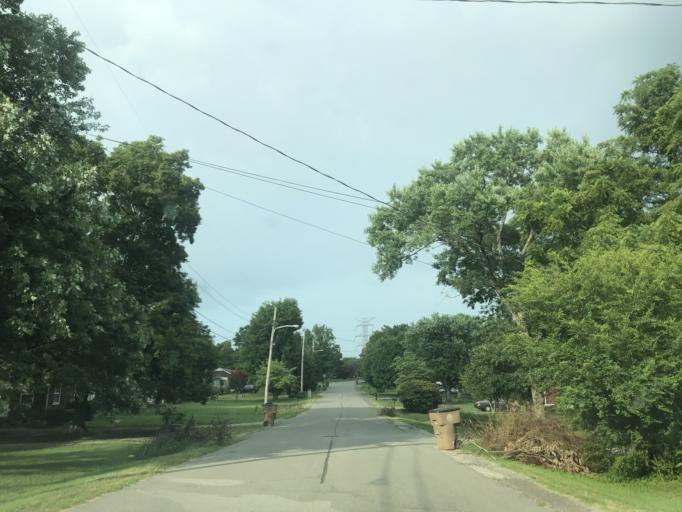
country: US
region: Tennessee
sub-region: Davidson County
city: Lakewood
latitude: 36.1596
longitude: -86.6768
